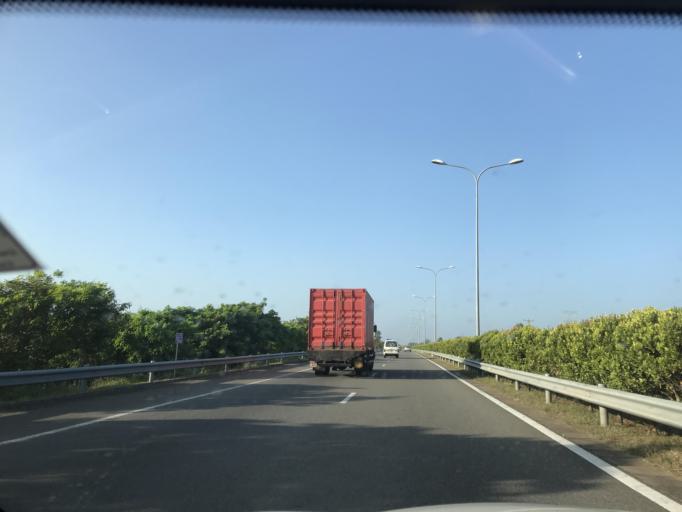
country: LK
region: Western
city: Ja Ela
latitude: 7.0665
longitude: 79.8787
